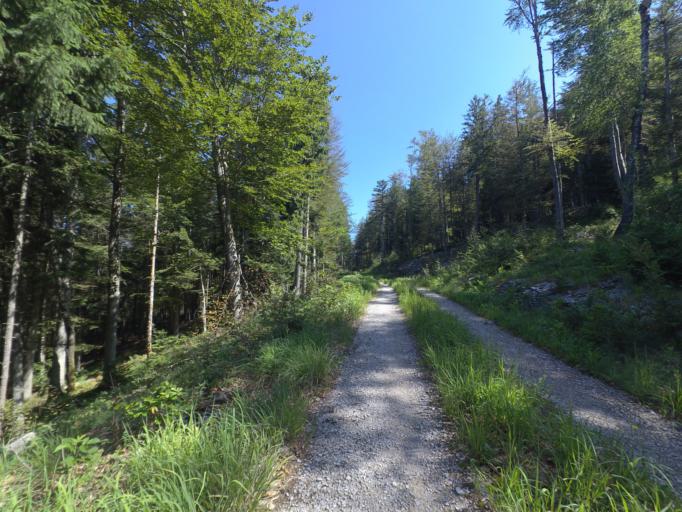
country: AT
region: Salzburg
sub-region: Politischer Bezirk Salzburg-Umgebung
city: Elsbethen
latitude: 47.7470
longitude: 13.1216
